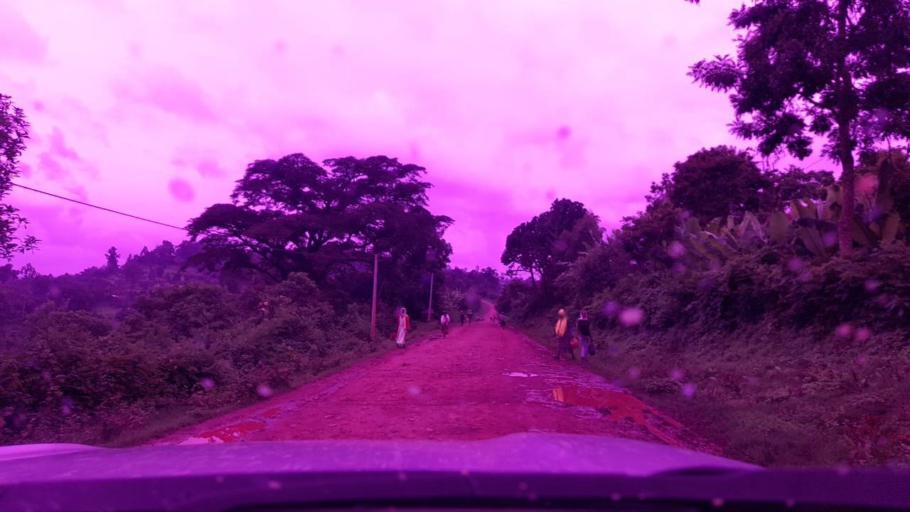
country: ET
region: Southern Nations, Nationalities, and People's Region
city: Bonga
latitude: 7.5532
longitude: 35.8573
